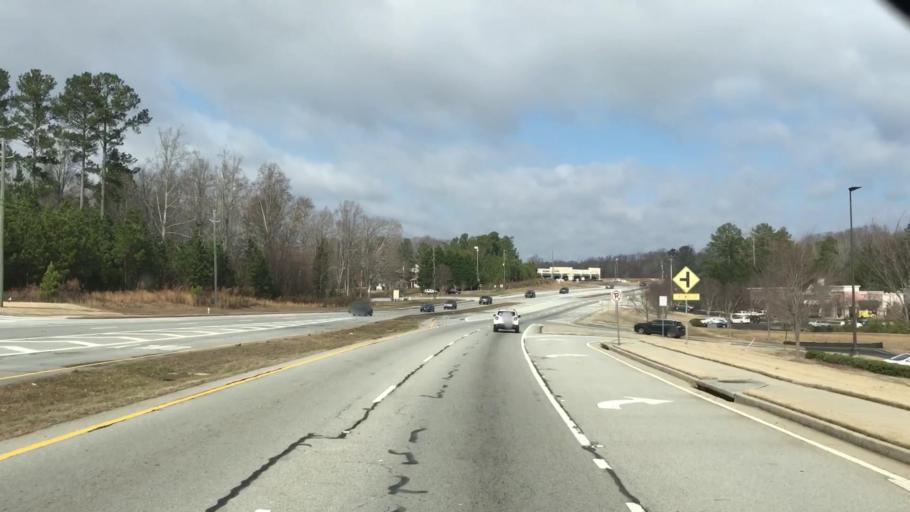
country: US
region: Georgia
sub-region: Hall County
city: Oakwood
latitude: 34.1965
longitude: -83.8590
